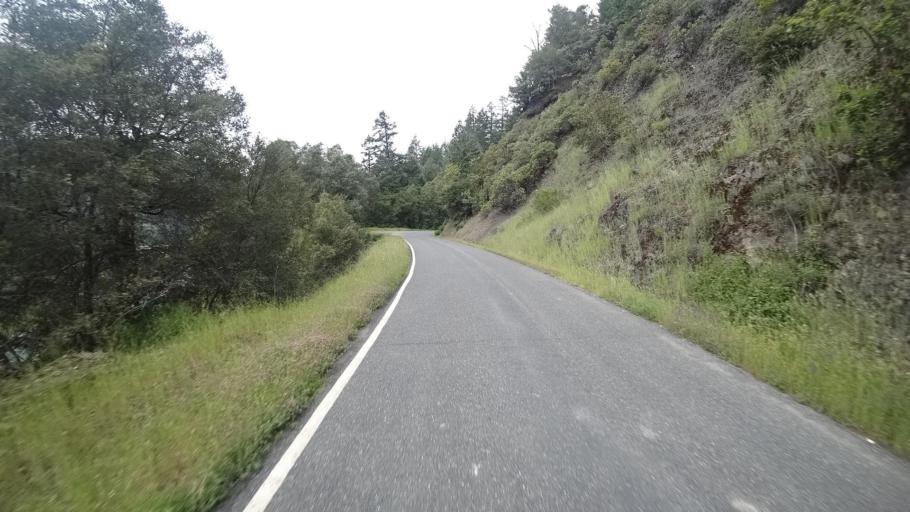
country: US
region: California
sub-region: Humboldt County
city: Willow Creek
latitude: 40.9496
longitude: -123.6179
